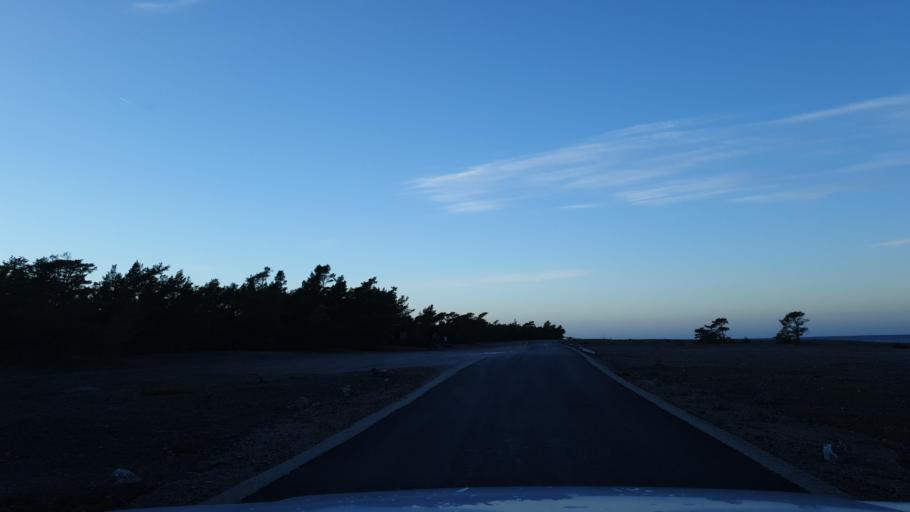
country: SE
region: Gotland
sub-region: Gotland
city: Slite
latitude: 57.9796
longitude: 19.1325
